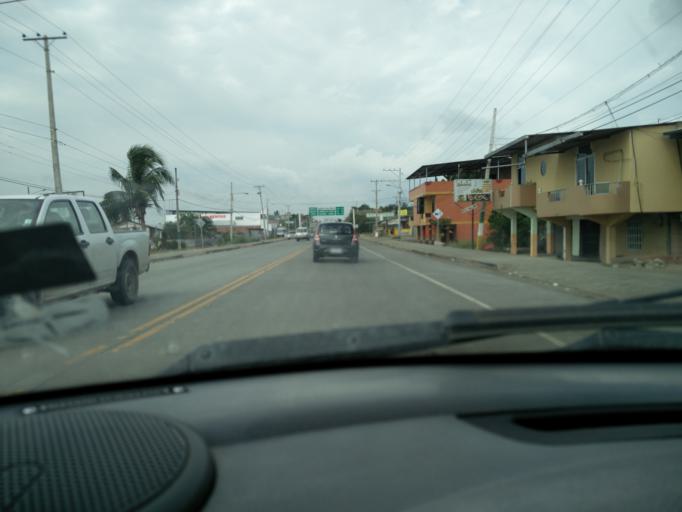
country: EC
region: Manabi
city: Rocafuerte
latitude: -0.9181
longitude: -80.4436
